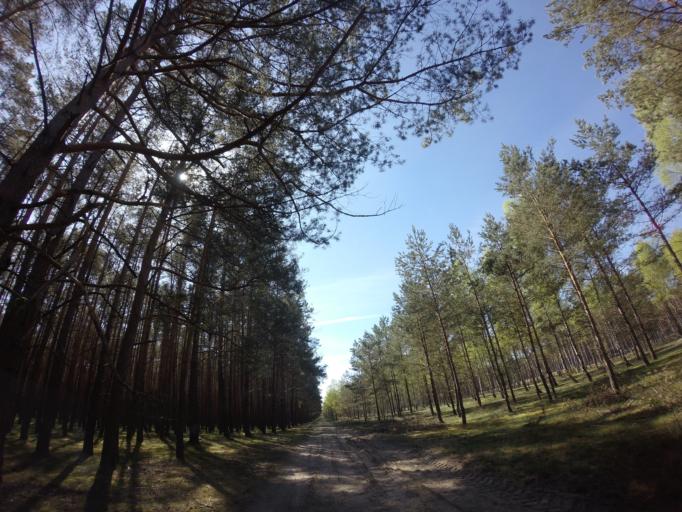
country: PL
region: West Pomeranian Voivodeship
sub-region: Powiat drawski
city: Kalisz Pomorski
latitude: 53.1983
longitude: 15.9388
